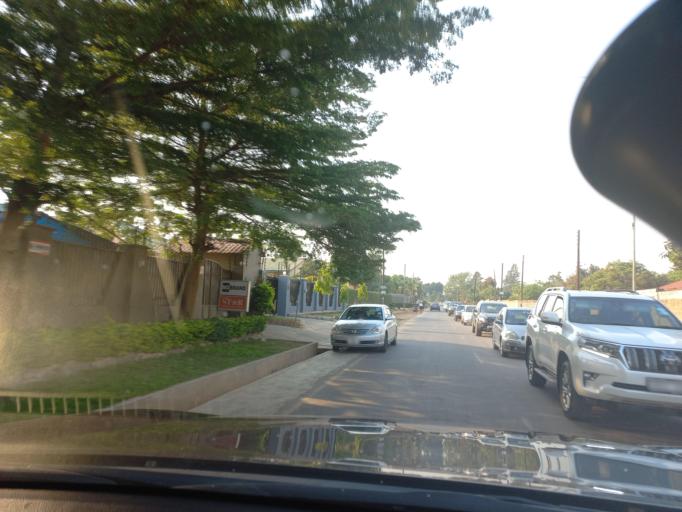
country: ZM
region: Lusaka
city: Lusaka
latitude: -15.4174
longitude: 28.3609
